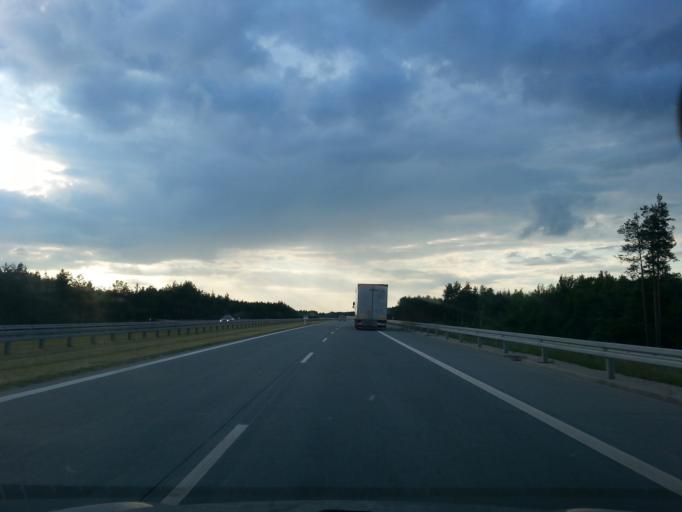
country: PL
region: Lodz Voivodeship
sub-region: Powiat zdunskowolski
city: Zdunska Wola
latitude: 51.5857
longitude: 18.8990
